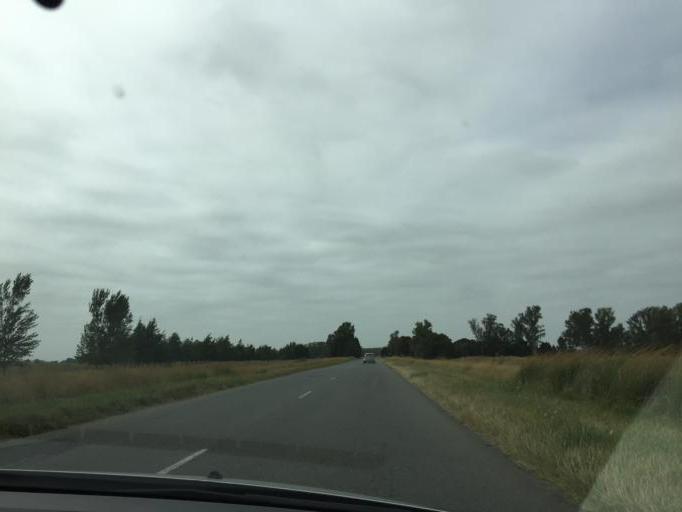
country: AR
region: Buenos Aires
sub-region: Partido de Las Flores
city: Las Flores
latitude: -36.2001
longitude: -59.0519
